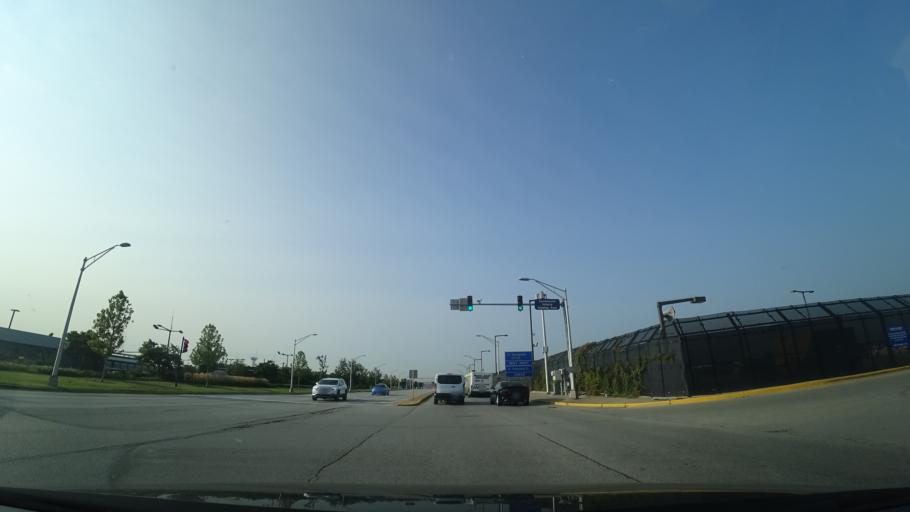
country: US
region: Illinois
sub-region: Cook County
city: Rosemont
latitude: 41.9823
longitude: -87.8857
